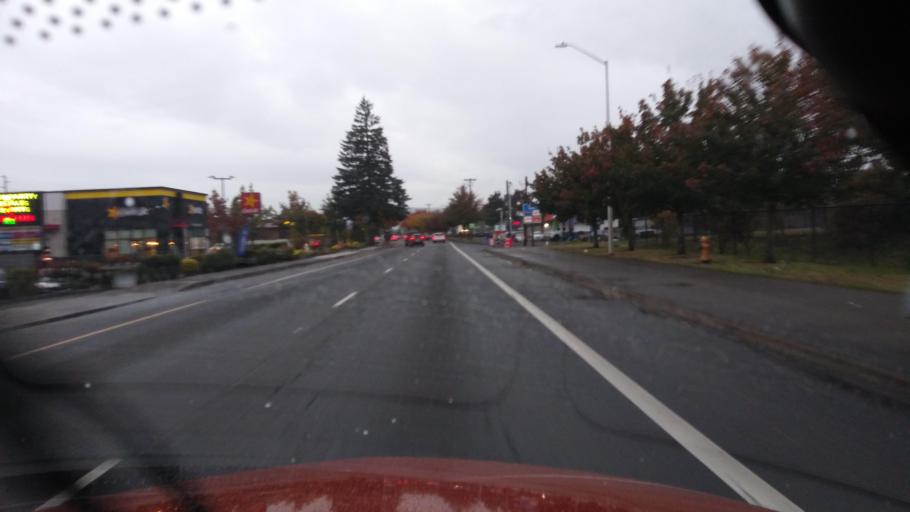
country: US
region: Oregon
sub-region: Washington County
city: Cornelius
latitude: 45.5210
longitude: -123.0691
